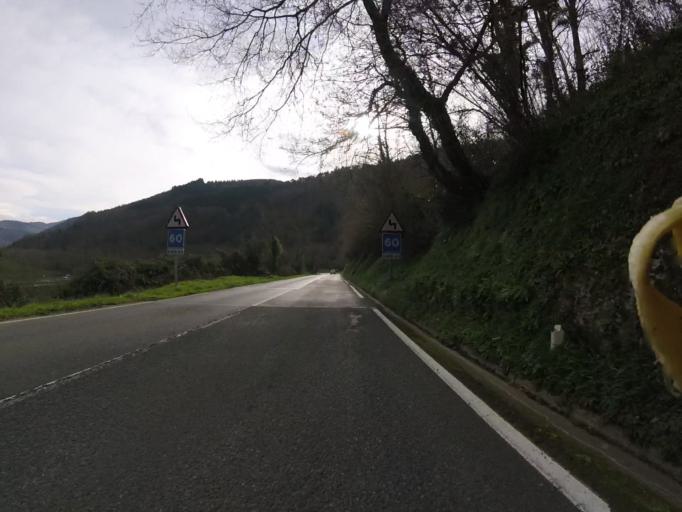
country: ES
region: Basque Country
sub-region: Provincia de Guipuzcoa
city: Cestona
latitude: 43.2550
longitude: -2.2553
